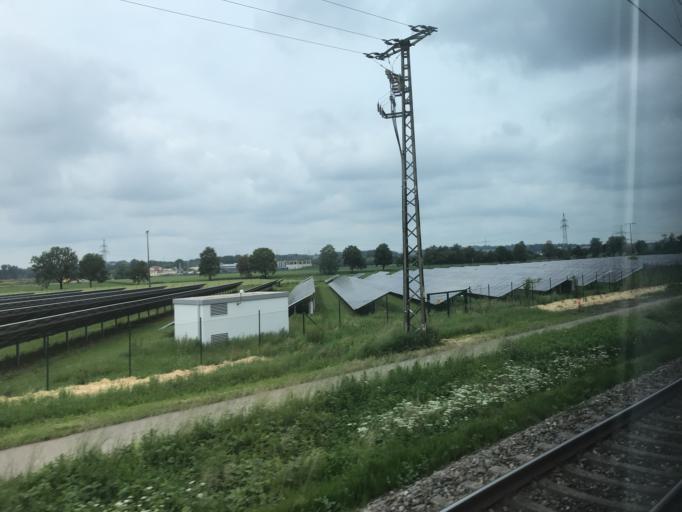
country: DE
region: Bavaria
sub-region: Swabia
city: Gundremmingen
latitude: 48.4694
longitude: 10.3930
